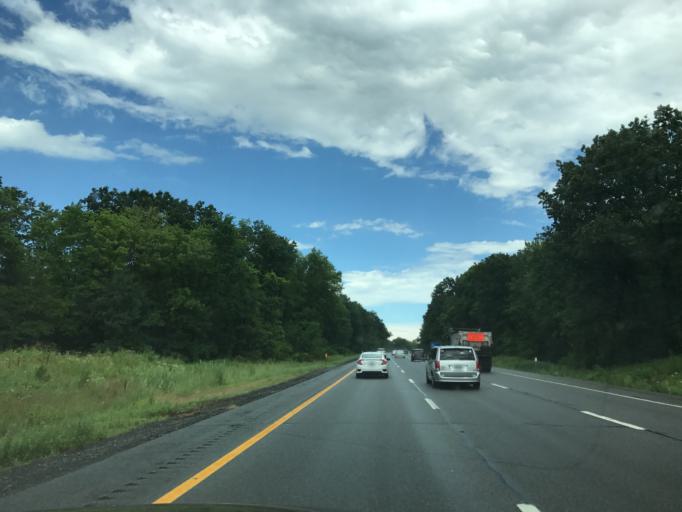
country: US
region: New York
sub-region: Albany County
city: Cohoes
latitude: 42.8085
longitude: -73.7655
